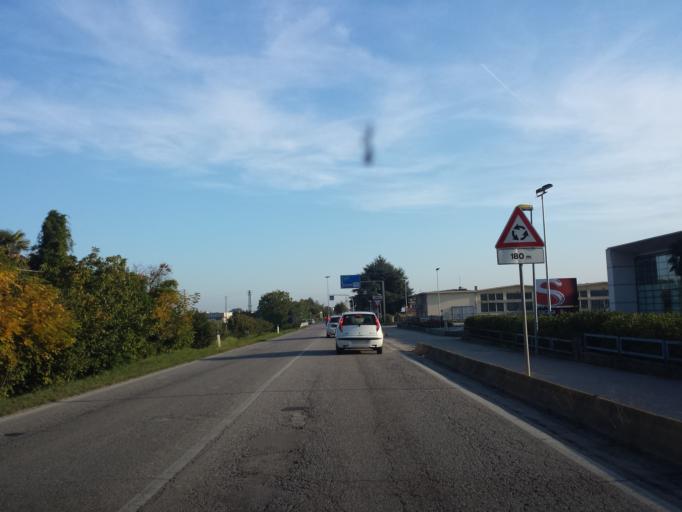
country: IT
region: Veneto
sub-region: Provincia di Vicenza
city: San Vito di Leguzzano
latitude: 45.6906
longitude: 11.3925
